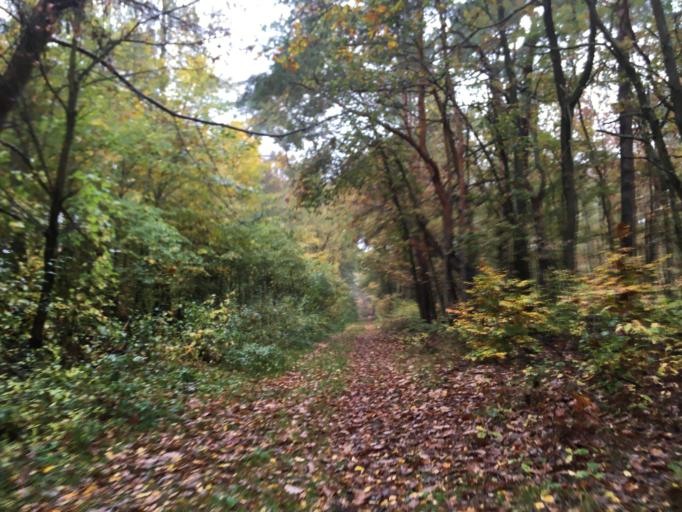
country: DE
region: Brandenburg
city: Briesen
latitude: 52.2622
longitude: 14.2946
